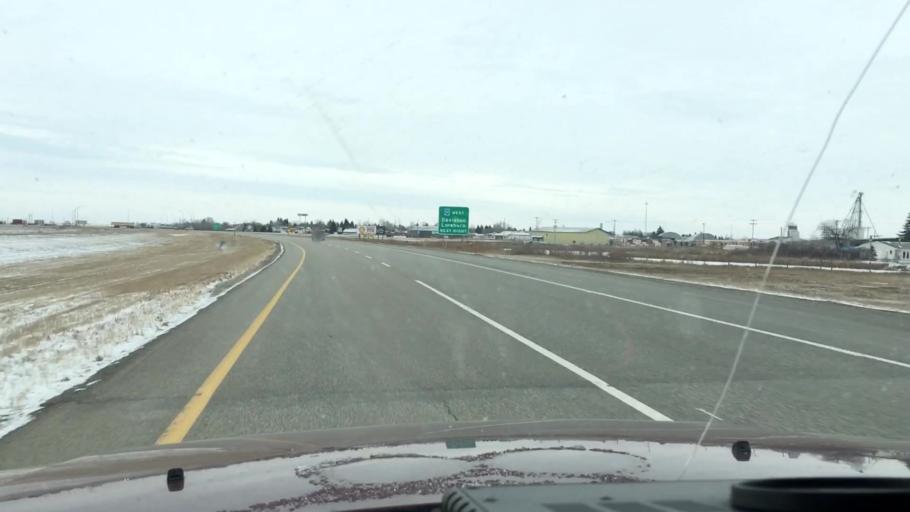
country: CA
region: Saskatchewan
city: Watrous
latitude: 51.2730
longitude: -106.0037
